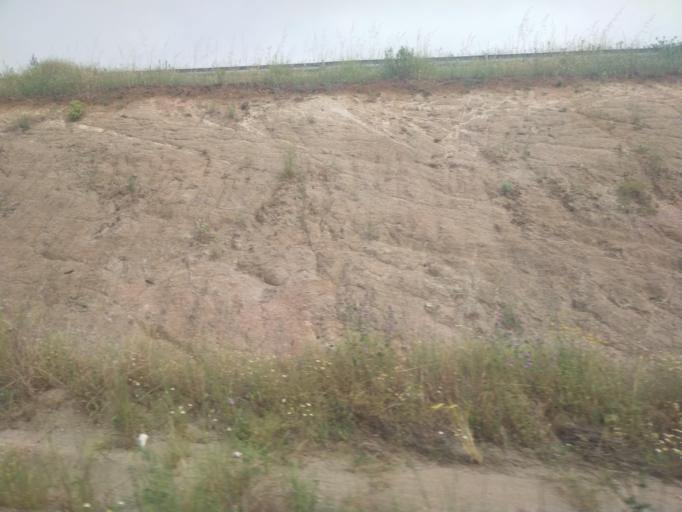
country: ES
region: Castille-La Mancha
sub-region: Province of Toledo
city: Polan
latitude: 39.7887
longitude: -4.1539
